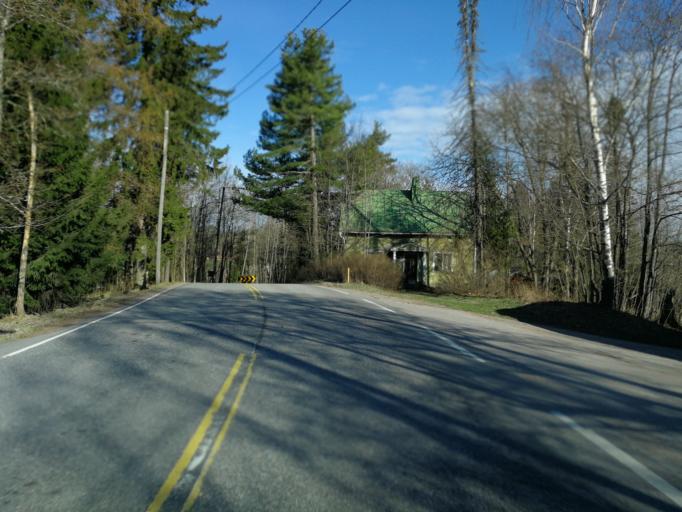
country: FI
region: Uusimaa
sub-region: Helsinki
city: Kirkkonummi
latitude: 60.2143
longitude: 24.4836
